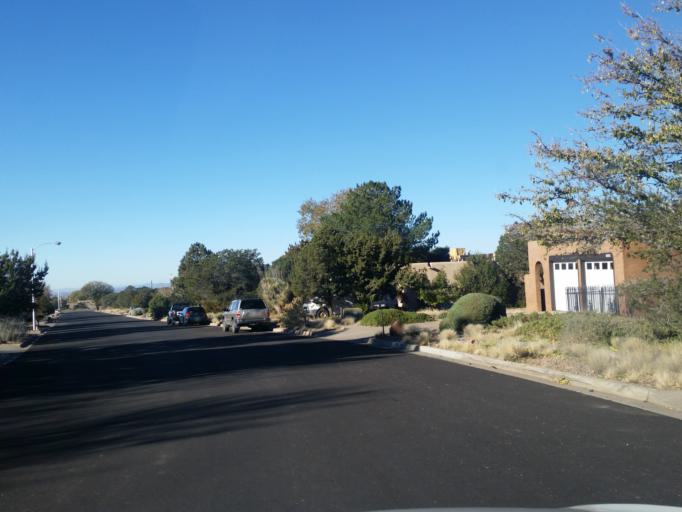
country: US
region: New Mexico
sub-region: Santa Fe County
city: Santa Fe
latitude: 35.6485
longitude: -105.9302
